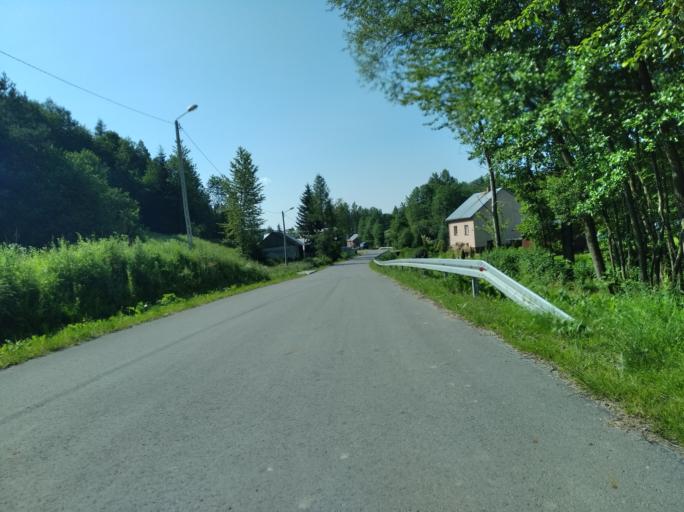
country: PL
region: Subcarpathian Voivodeship
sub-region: Powiat brzozowski
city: Nozdrzec
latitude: 49.8241
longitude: 22.1629
